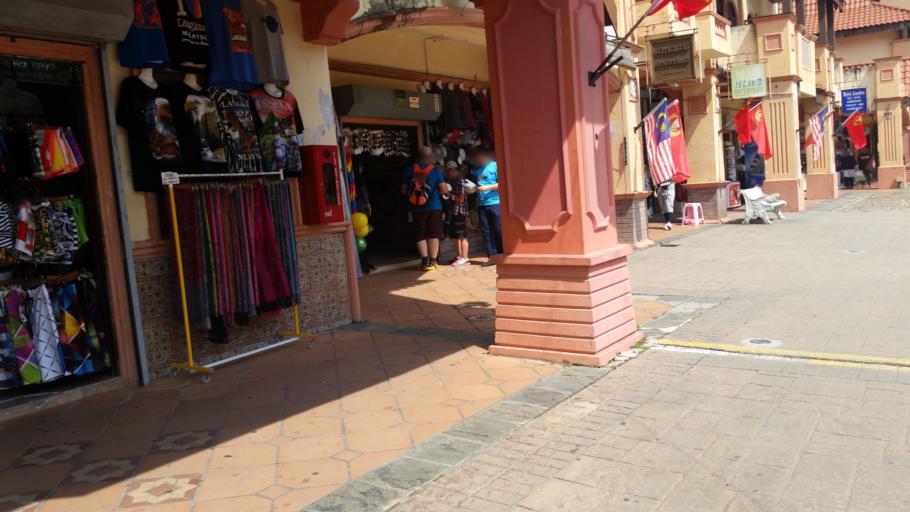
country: MY
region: Kedah
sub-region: Langkawi
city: Kuah
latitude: 6.3706
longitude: 99.6719
